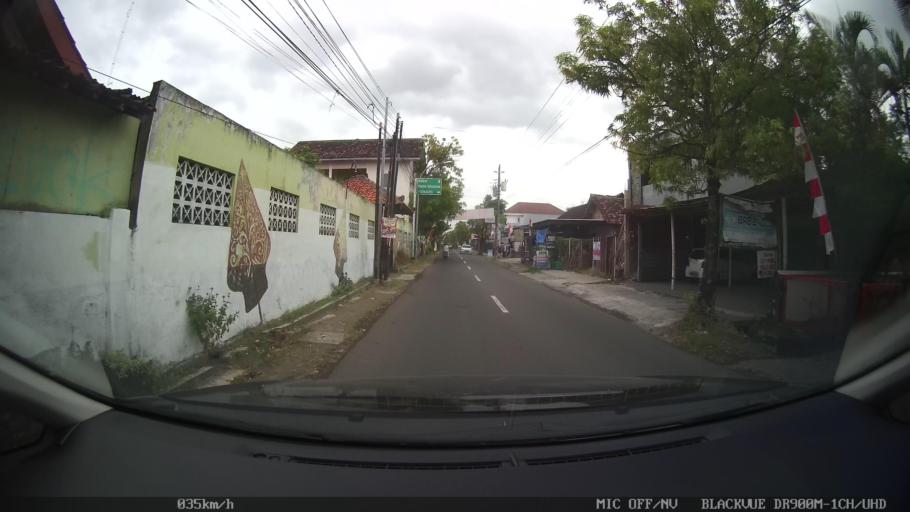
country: ID
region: Daerah Istimewa Yogyakarta
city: Depok
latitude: -7.8201
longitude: 110.4155
